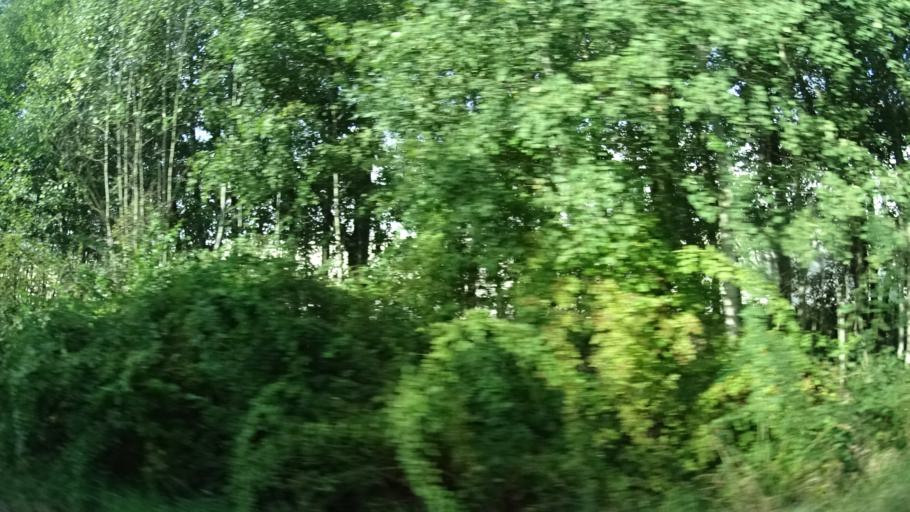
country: DE
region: Hesse
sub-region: Regierungsbezirk Kassel
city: Neuhof
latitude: 50.4567
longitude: 9.5991
